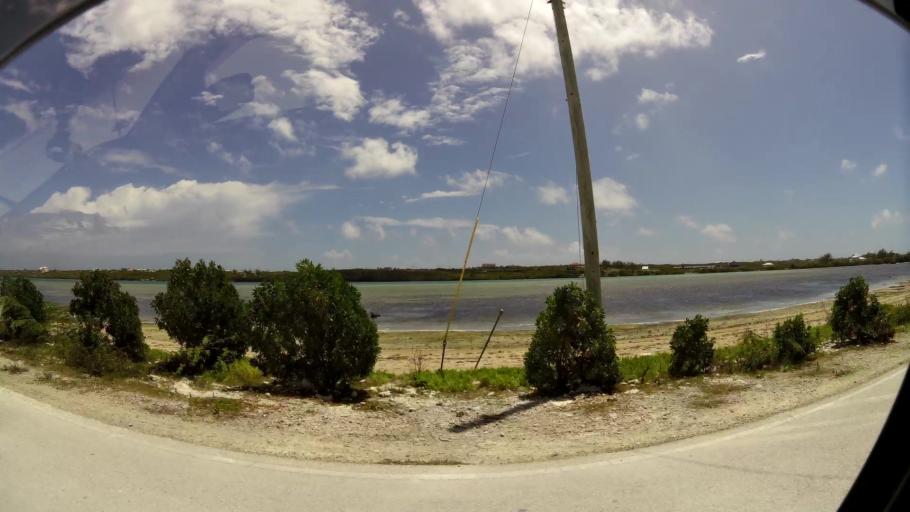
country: TC
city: Cockburn Town
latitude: 21.4855
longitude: -71.1424
